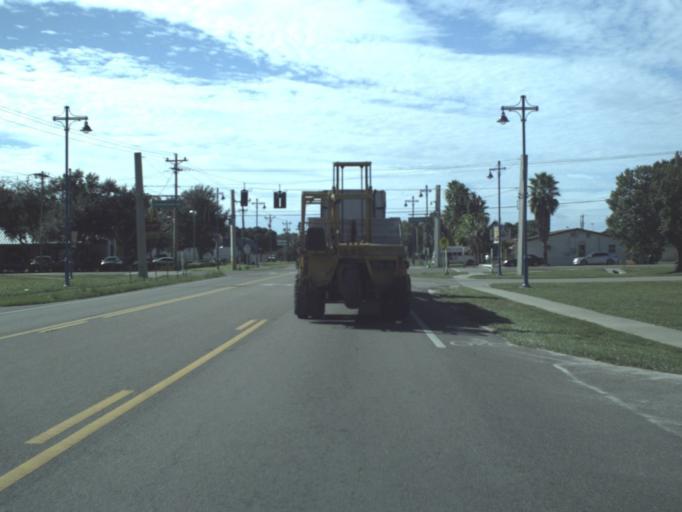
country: US
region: Florida
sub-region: Collier County
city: Immokalee
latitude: 26.4266
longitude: -81.4338
